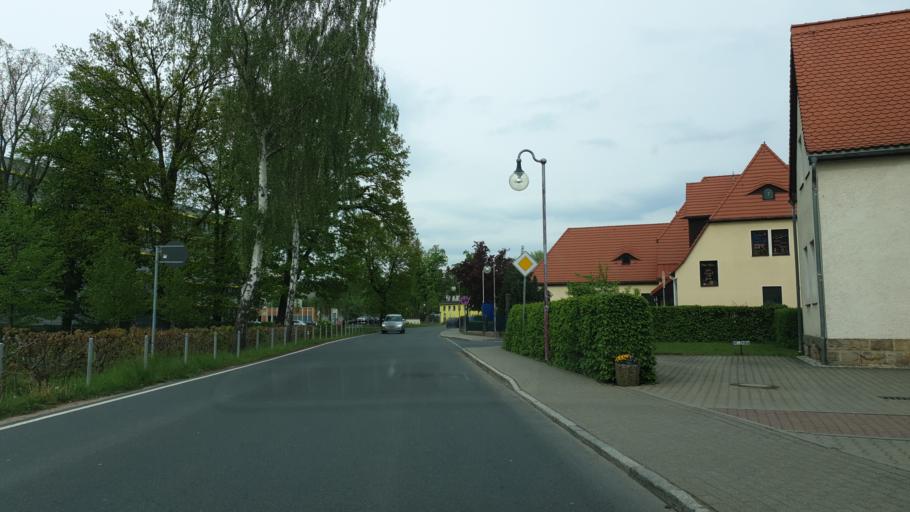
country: DE
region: Saxony
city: Dippoldiswalde
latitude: 50.8971
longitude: 13.6623
